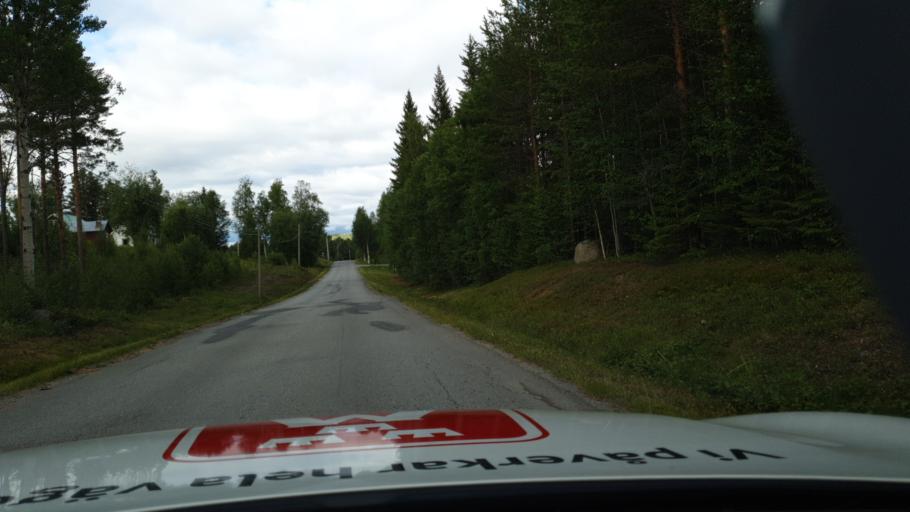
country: SE
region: Vaesterbotten
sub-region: Dorotea Kommun
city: Dorotea
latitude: 63.9155
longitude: 16.3248
